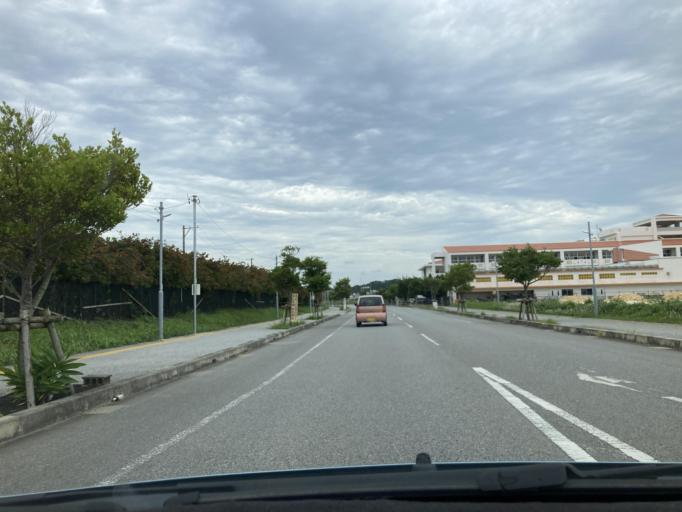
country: JP
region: Okinawa
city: Okinawa
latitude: 26.3944
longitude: 127.7410
